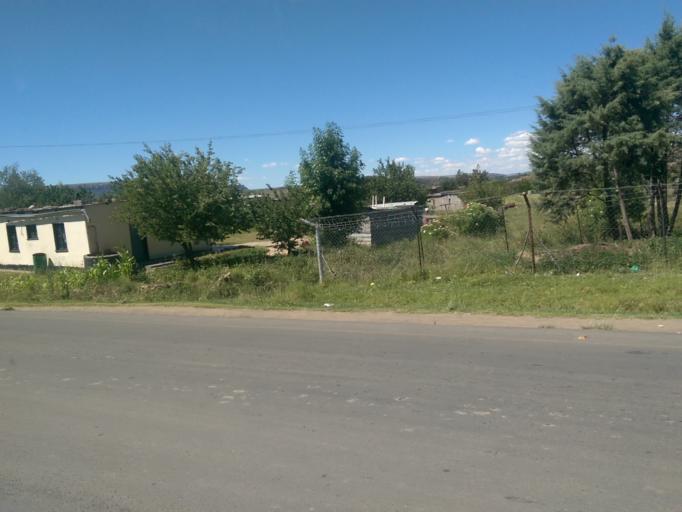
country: LS
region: Maseru
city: Maseru
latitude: -29.4140
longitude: 27.5584
